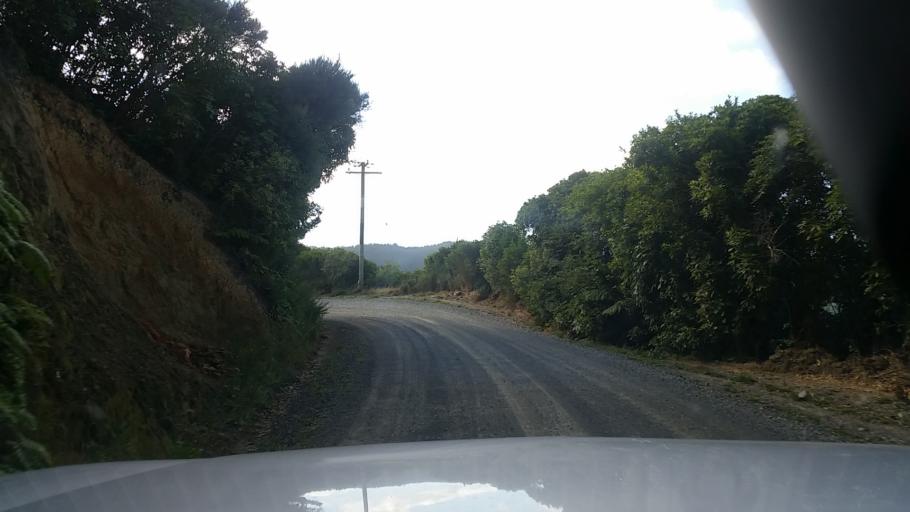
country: NZ
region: Marlborough
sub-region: Marlborough District
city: Picton
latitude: -41.2868
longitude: 174.1318
